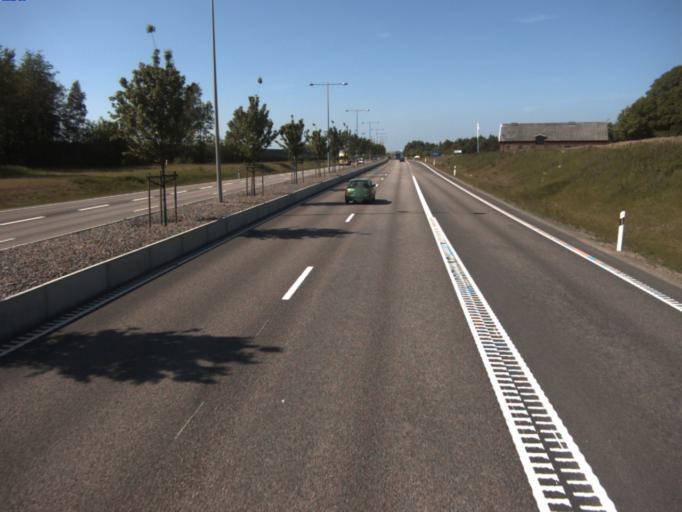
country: SE
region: Skane
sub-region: Helsingborg
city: Odakra
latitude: 56.0565
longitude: 12.7498
